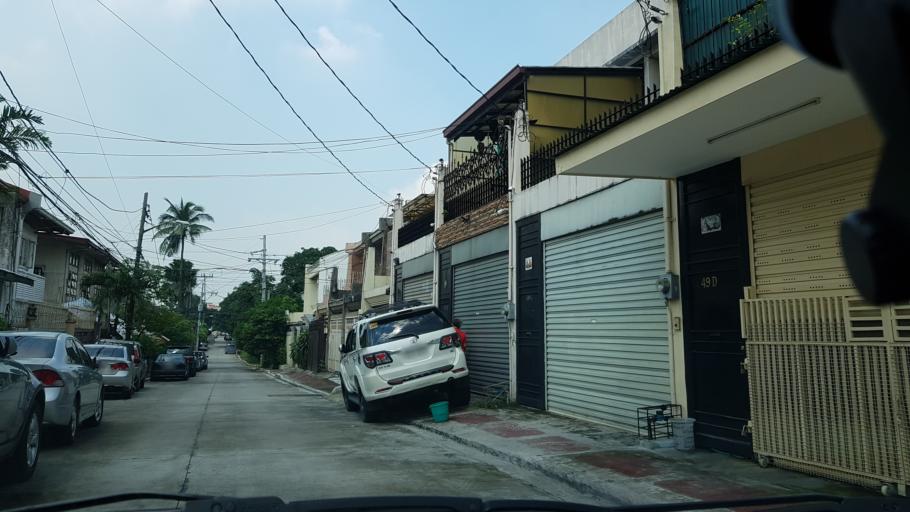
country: PH
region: Calabarzon
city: Del Monte
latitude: 14.6313
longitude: 121.0288
